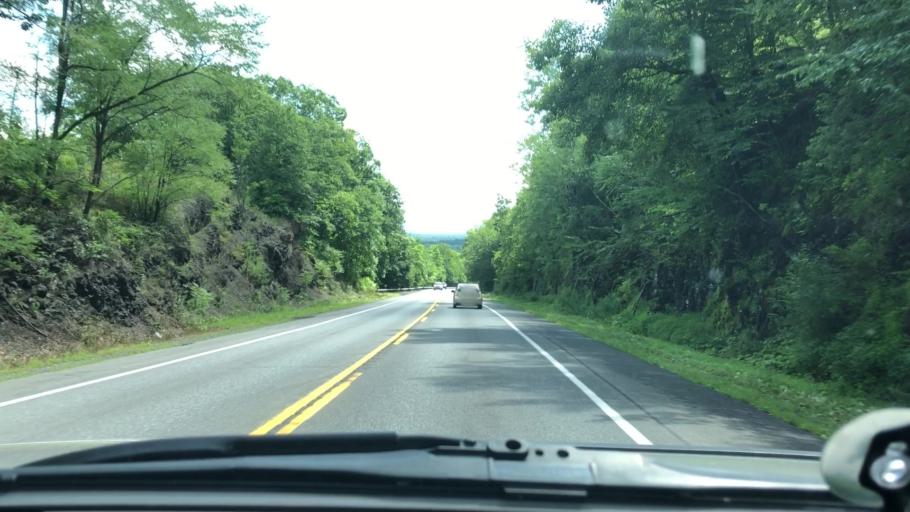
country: US
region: New York
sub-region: Ulster County
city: Saugerties
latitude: 42.1182
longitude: -73.9849
